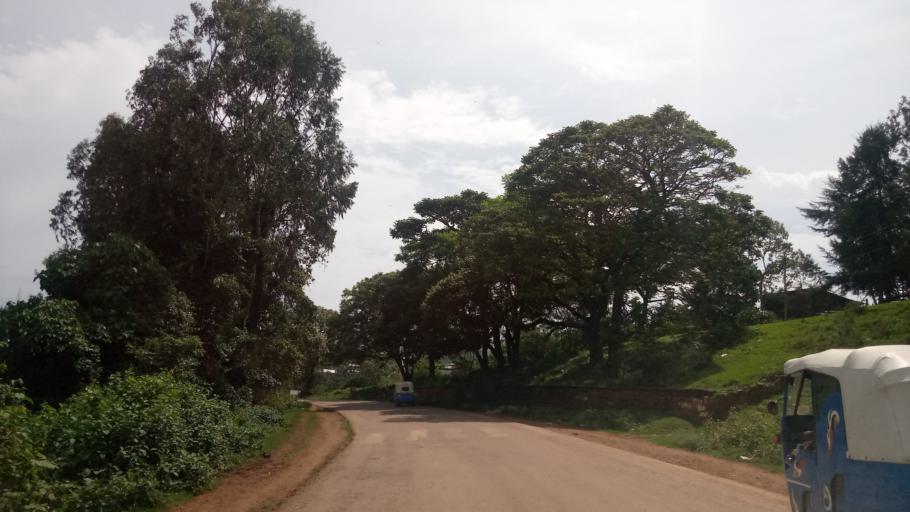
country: ET
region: Oromiya
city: Agaro
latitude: 7.8536
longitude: 36.5950
